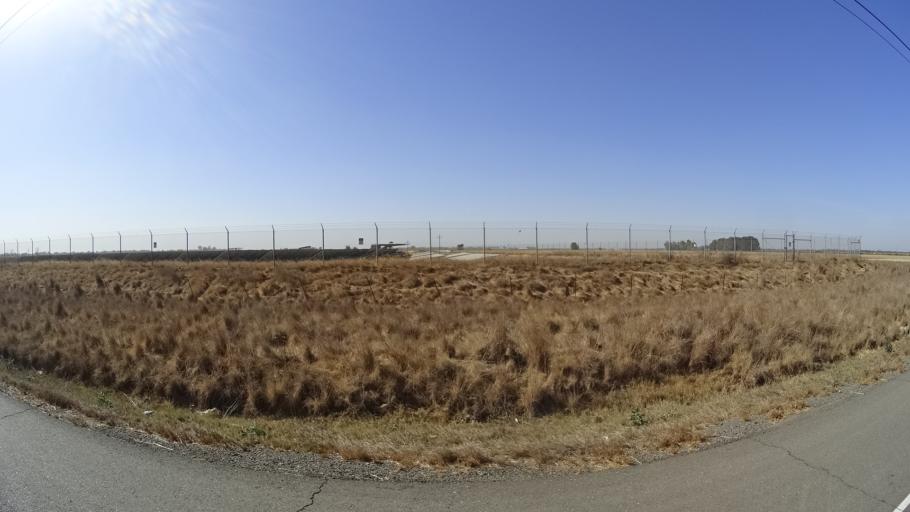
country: US
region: California
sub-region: Yolo County
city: Davis
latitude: 38.5840
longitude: -121.7304
